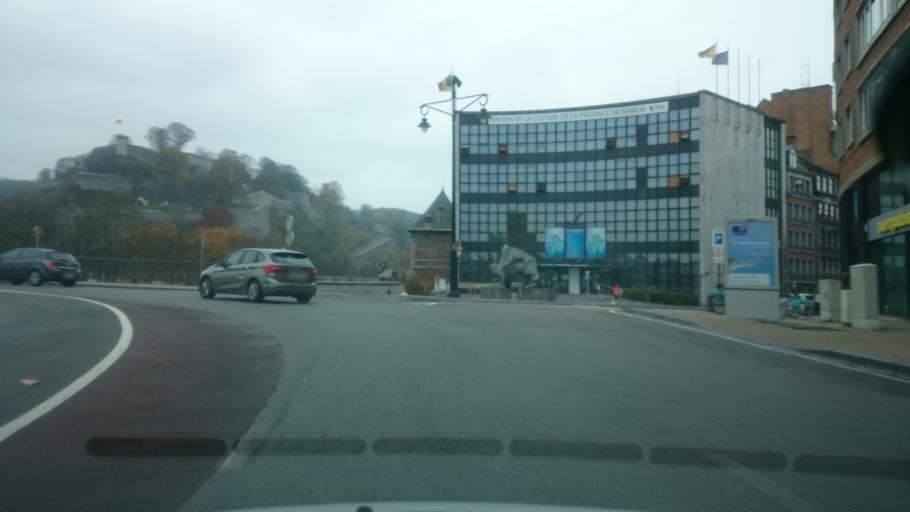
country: BE
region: Wallonia
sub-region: Province de Namur
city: Namur
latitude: 50.4625
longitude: 4.8700
